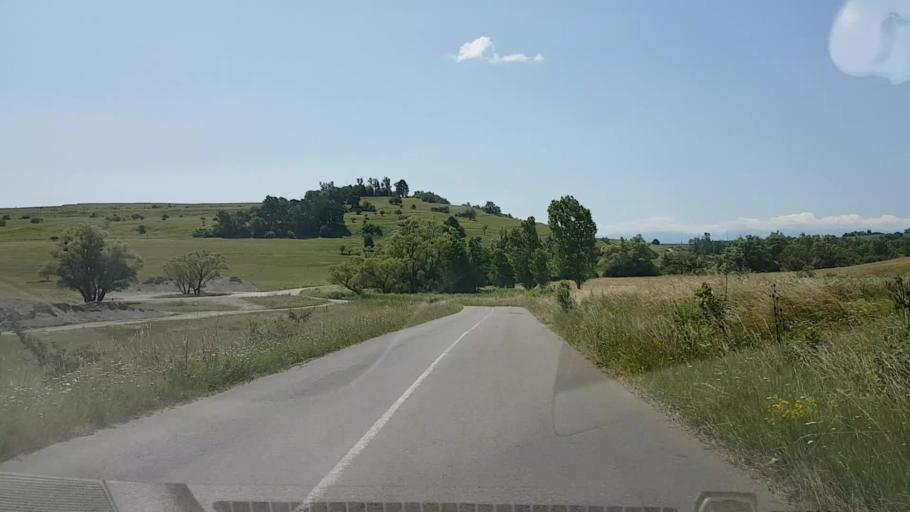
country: RO
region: Brasov
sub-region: Comuna Cincu
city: Cincu
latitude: 45.9536
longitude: 24.7826
